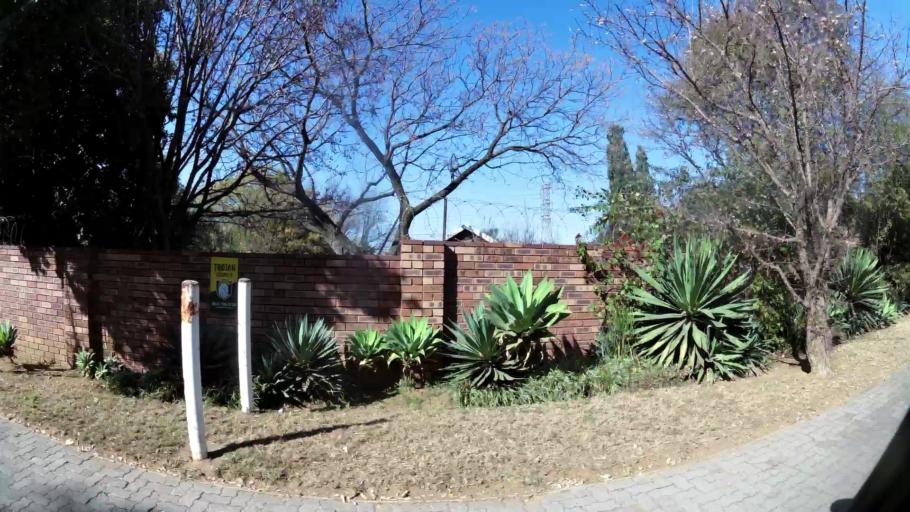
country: ZA
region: Gauteng
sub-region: City of Johannesburg Metropolitan Municipality
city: Roodepoort
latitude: -26.1075
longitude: 27.9611
